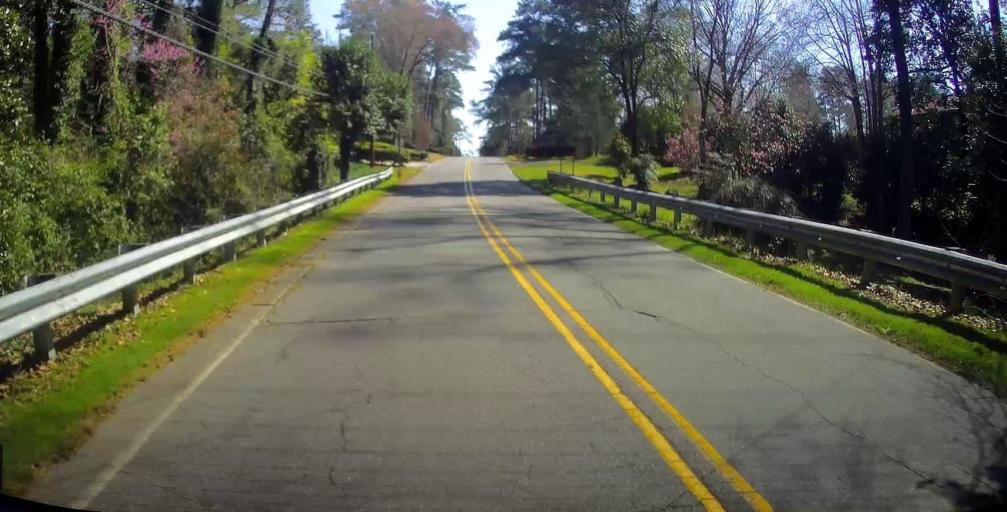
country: US
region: Georgia
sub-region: Bibb County
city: Macon
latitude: 32.8566
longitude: -83.6311
